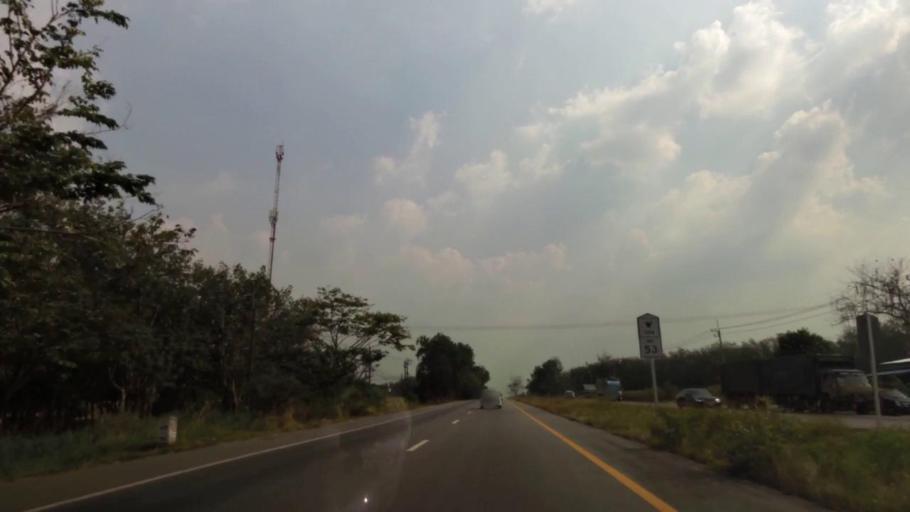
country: TH
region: Chon Buri
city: Nong Yai
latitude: 13.1121
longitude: 101.3752
